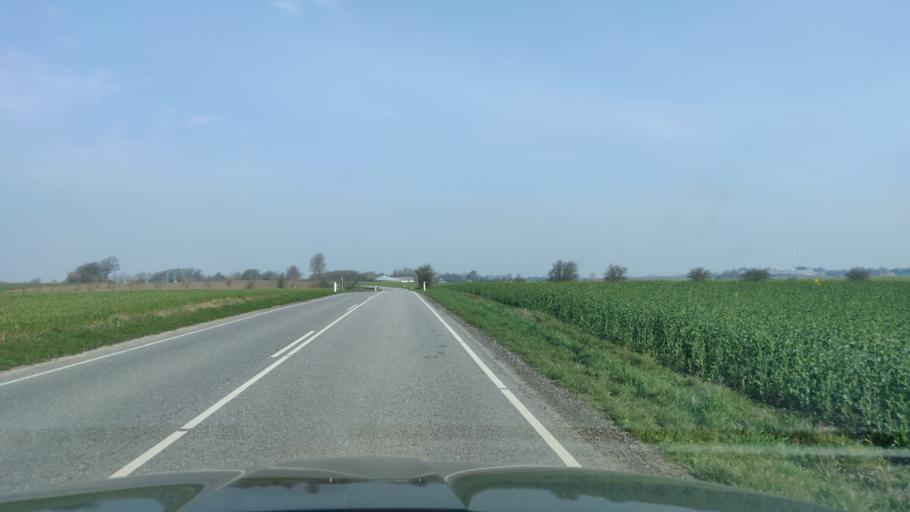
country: DK
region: South Denmark
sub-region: Nordfyns Kommune
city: Sonderso
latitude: 55.5025
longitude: 10.2498
